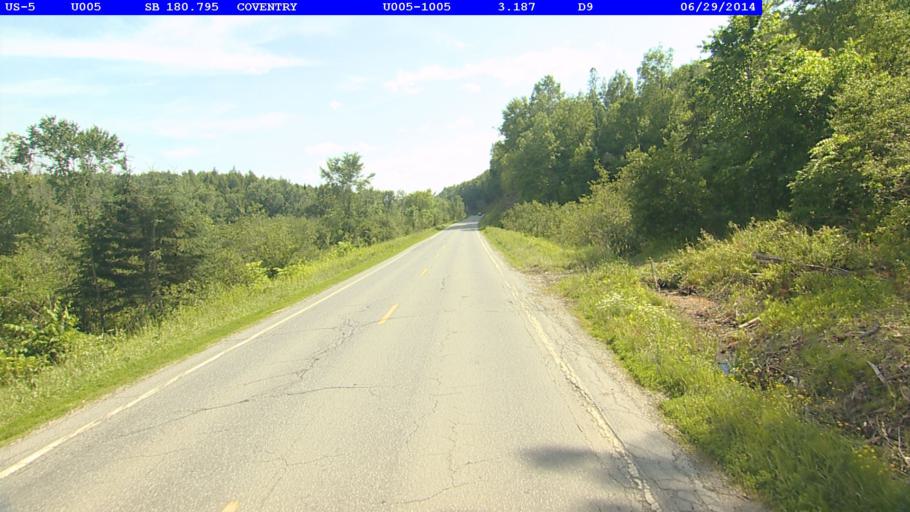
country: US
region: Vermont
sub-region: Orleans County
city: Newport
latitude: 44.9006
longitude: -72.2437
